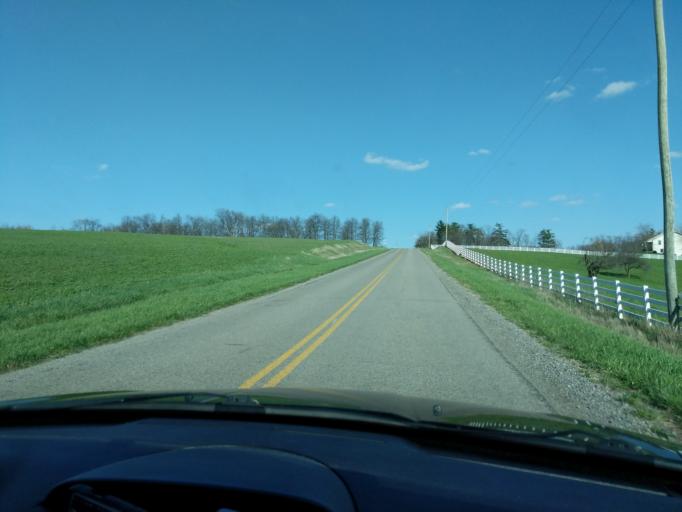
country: US
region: Ohio
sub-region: Logan County
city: De Graff
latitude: 40.2651
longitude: -83.8782
